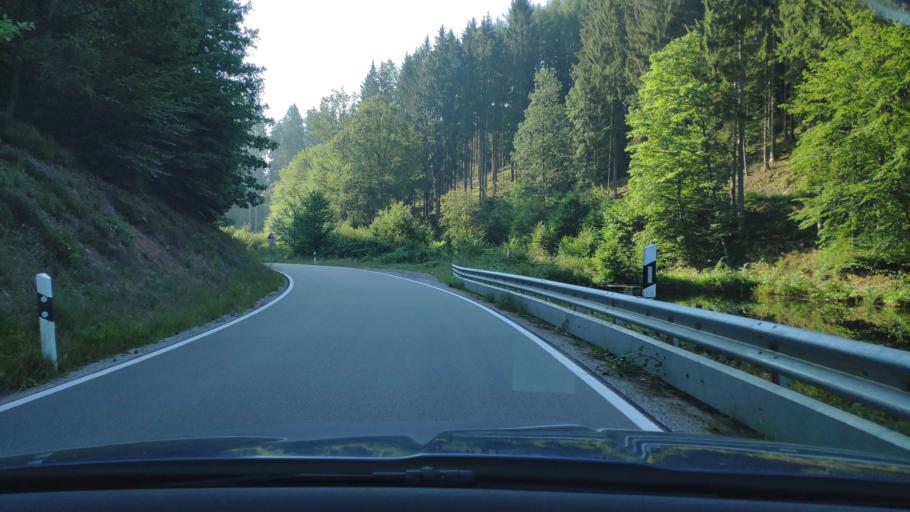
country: DE
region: Rheinland-Pfalz
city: Ludwigswinkel
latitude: 49.1022
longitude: 7.6226
